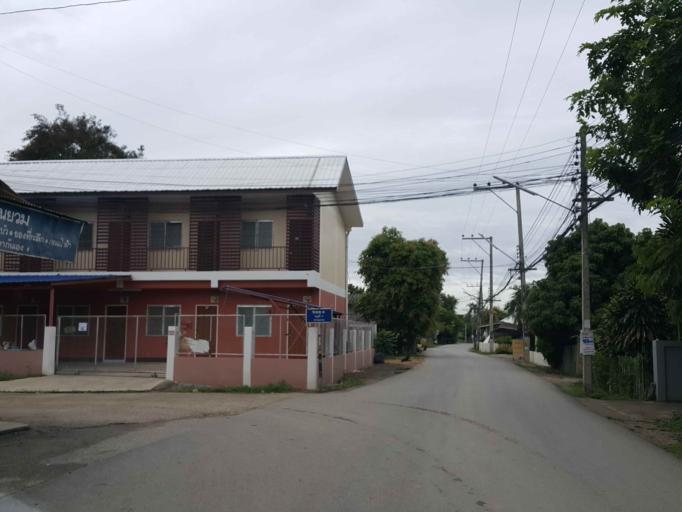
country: TH
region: Chiang Mai
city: Saraphi
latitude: 18.7560
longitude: 99.0485
